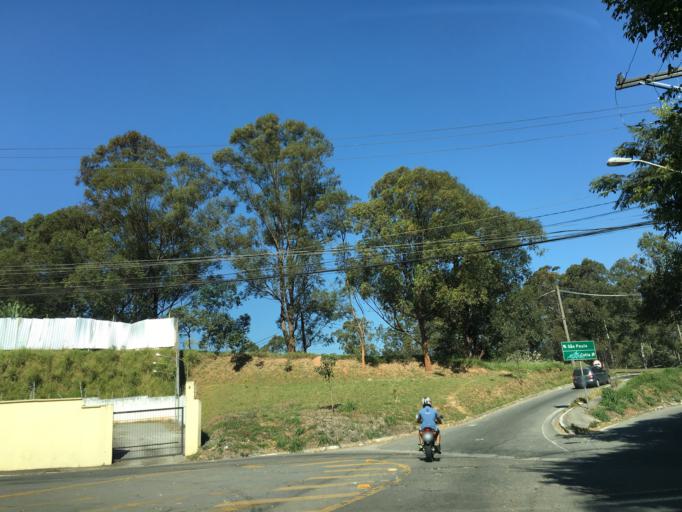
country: BR
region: Sao Paulo
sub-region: Taboao Da Serra
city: Taboao da Serra
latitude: -23.5844
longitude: -46.7622
